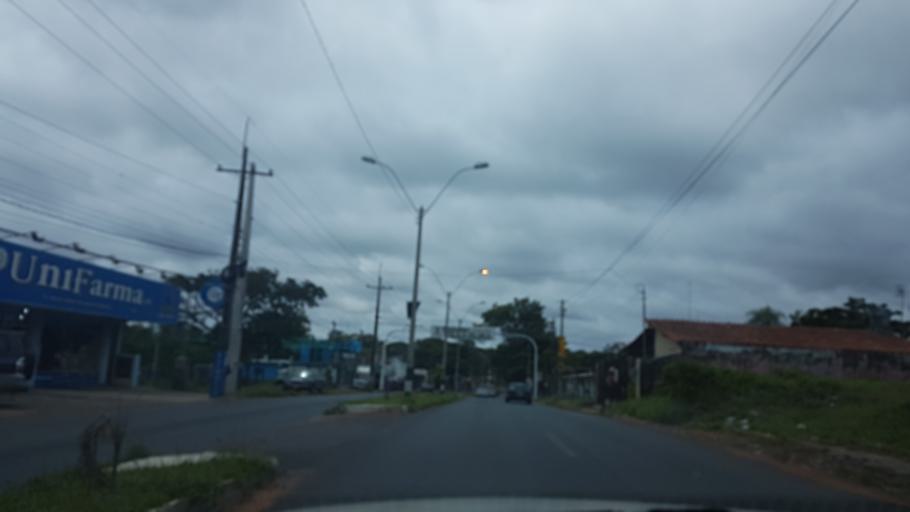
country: PY
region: Central
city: Villa Elisa
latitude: -25.3936
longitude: -57.5820
